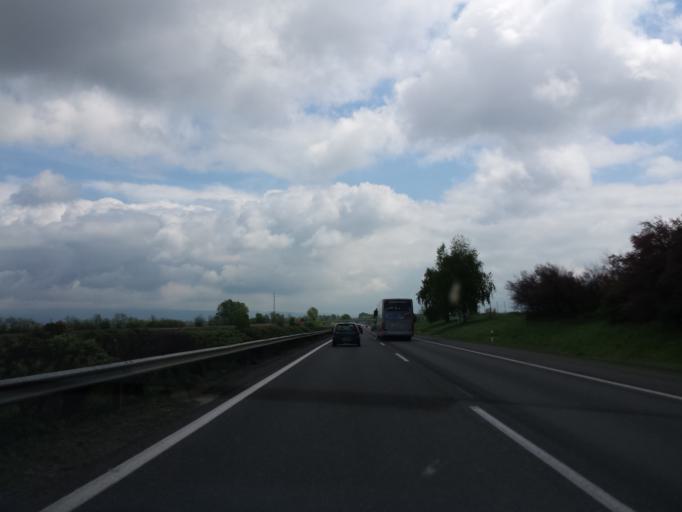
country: HU
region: Komarom-Esztergom
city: Kocs
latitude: 47.6338
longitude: 18.2454
